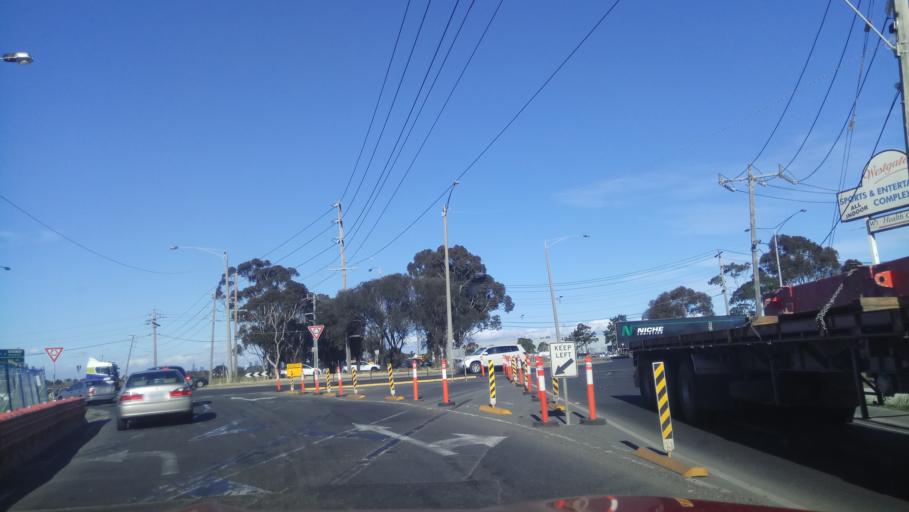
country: AU
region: Victoria
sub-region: Hobsons Bay
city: Altona North
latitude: -37.8315
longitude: 144.8259
